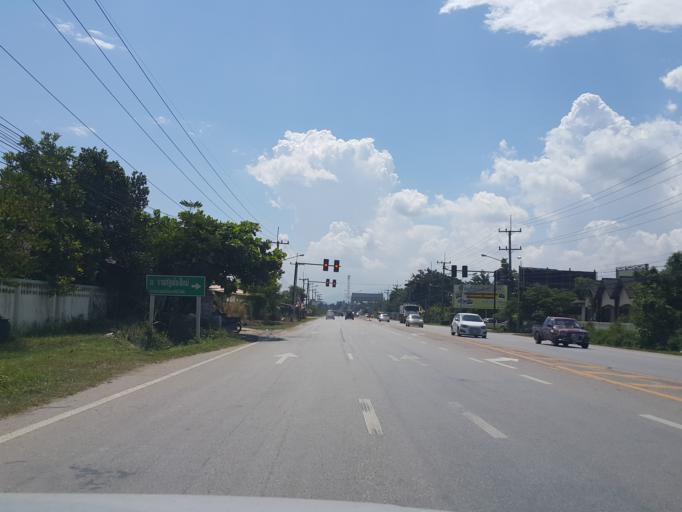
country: TH
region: Chiang Mai
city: Mae Taeng
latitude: 19.0263
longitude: 98.9449
